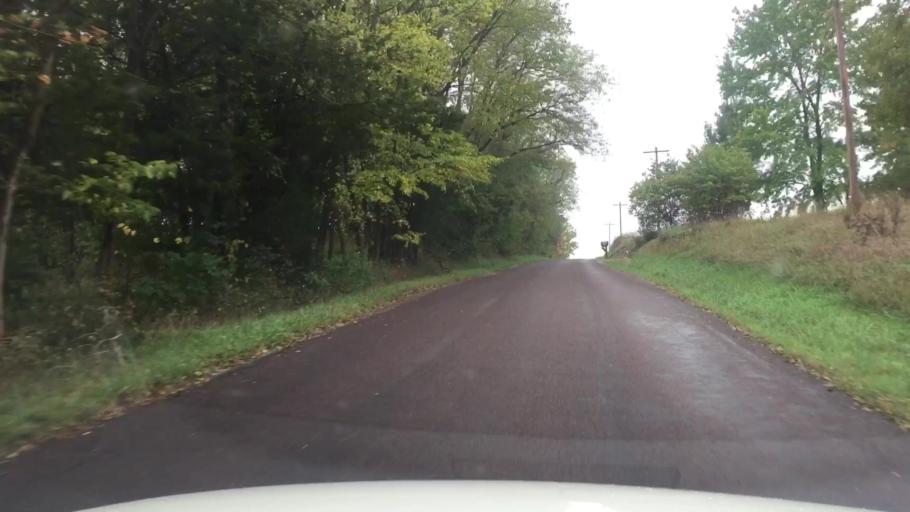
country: US
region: Missouri
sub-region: Boone County
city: Columbia
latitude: 38.8560
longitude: -92.3559
